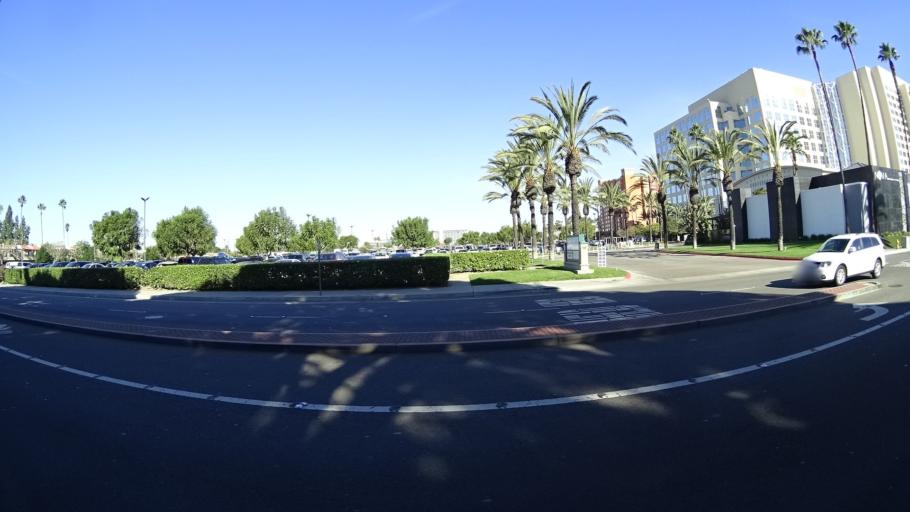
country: US
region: California
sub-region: Orange County
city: Garden Grove
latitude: 33.7886
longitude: -117.9179
